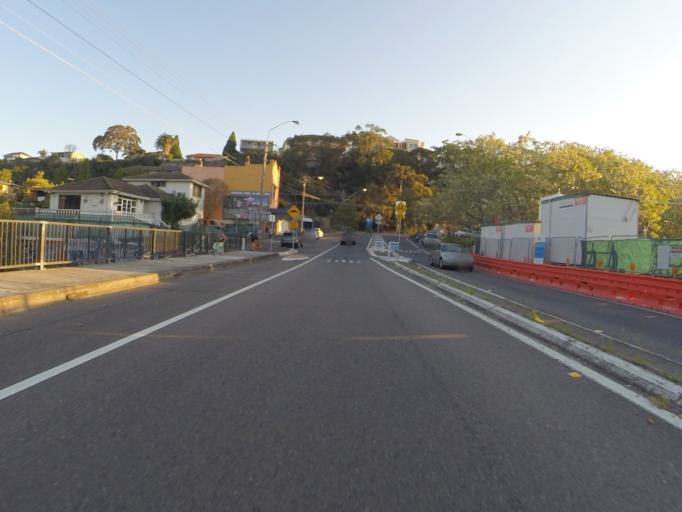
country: AU
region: New South Wales
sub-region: Rockdale
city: Bardwell Valley
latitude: -33.9226
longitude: 151.1428
